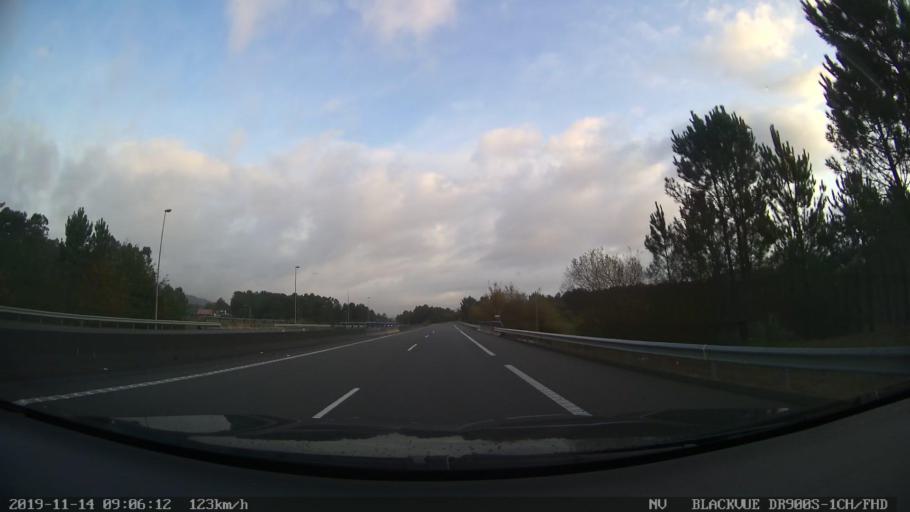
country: ES
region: Galicia
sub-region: Provincia de Pontevedra
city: Porrino
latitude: 42.1221
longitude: -8.6399
